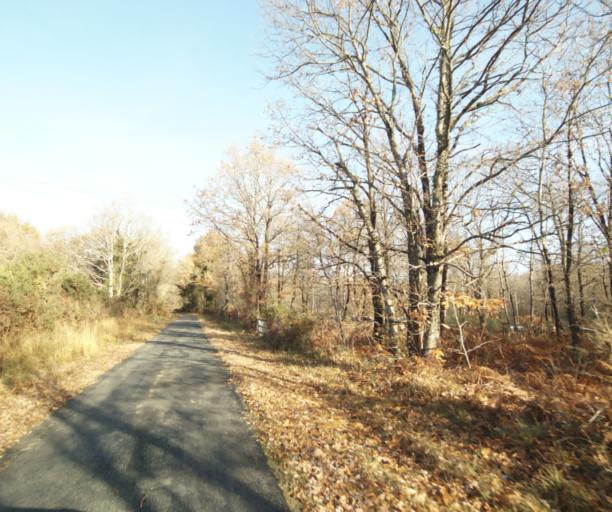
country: FR
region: Poitou-Charentes
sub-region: Departement de la Charente-Maritime
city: Burie
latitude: 45.7521
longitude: -0.4825
